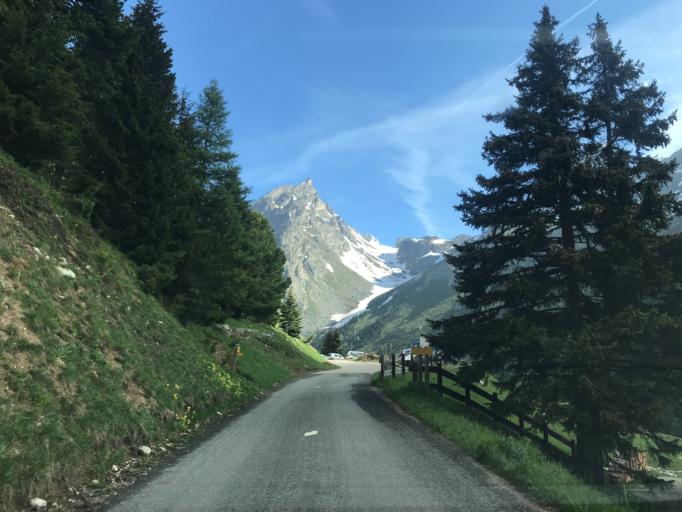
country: FR
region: Rhone-Alpes
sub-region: Departement de la Savoie
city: Modane
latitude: 45.2290
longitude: 6.6725
